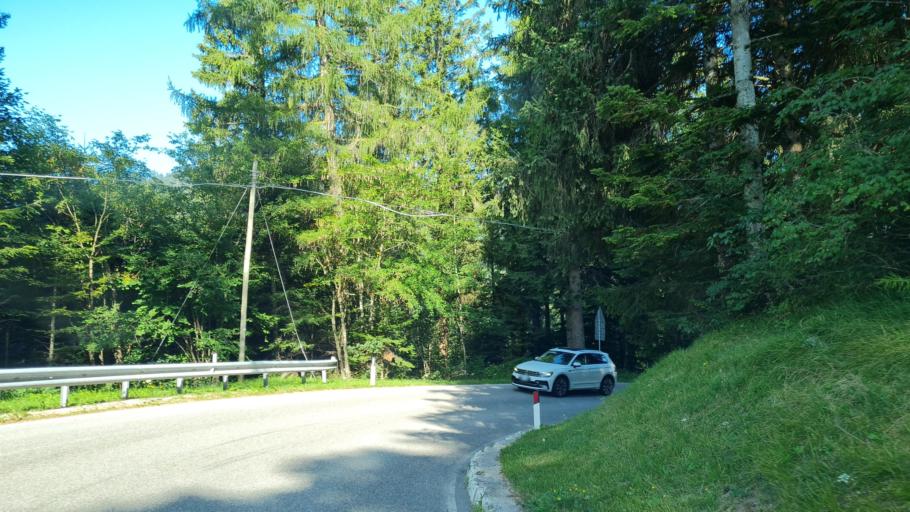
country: IT
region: Trentino-Alto Adige
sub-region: Provincia di Trento
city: Gionghi-Cappella
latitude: 45.9599
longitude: 11.2981
